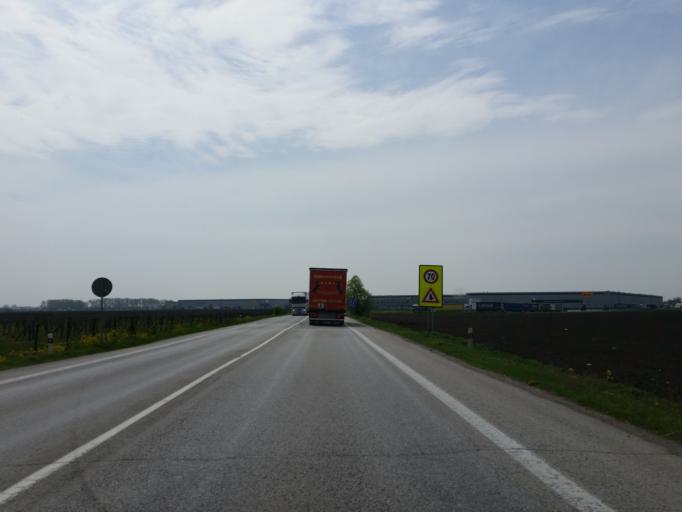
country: SK
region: Trnavsky
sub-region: Okres Galanta
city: Galanta
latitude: 48.2406
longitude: 17.7343
